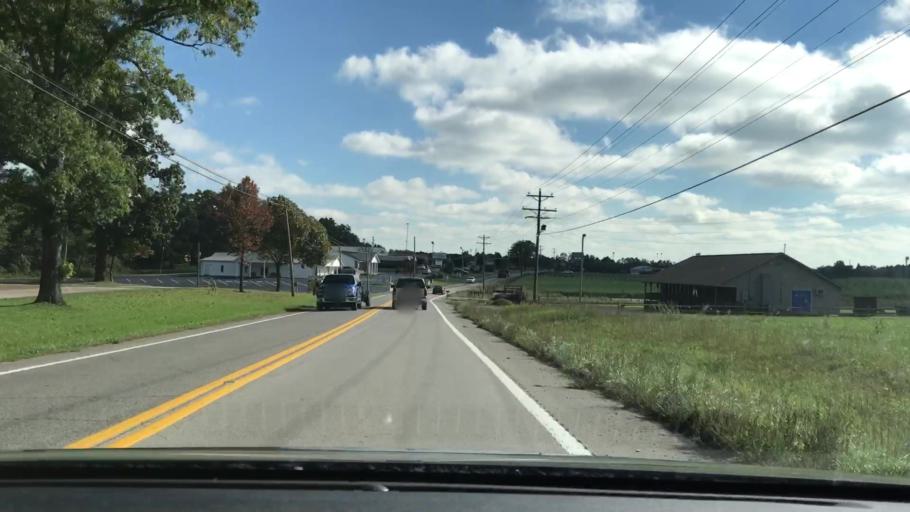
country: US
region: Tennessee
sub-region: Fentress County
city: Grimsley
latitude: 36.1926
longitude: -85.0204
